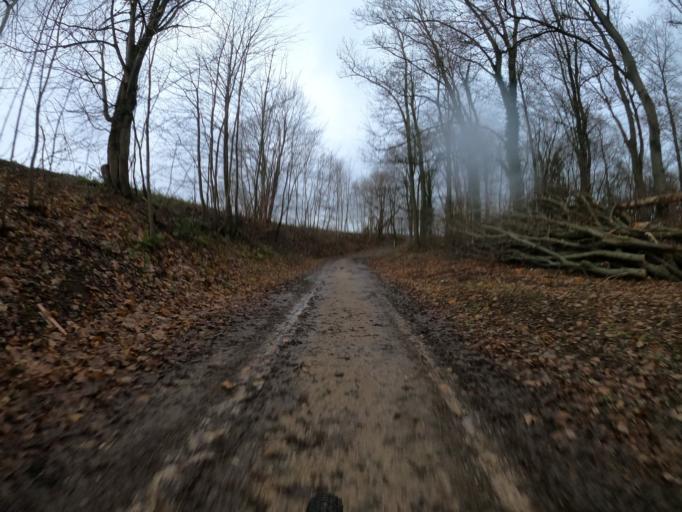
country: DE
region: Baden-Wuerttemberg
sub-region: Regierungsbezirk Stuttgart
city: Sussen
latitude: 48.6978
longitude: 9.7677
